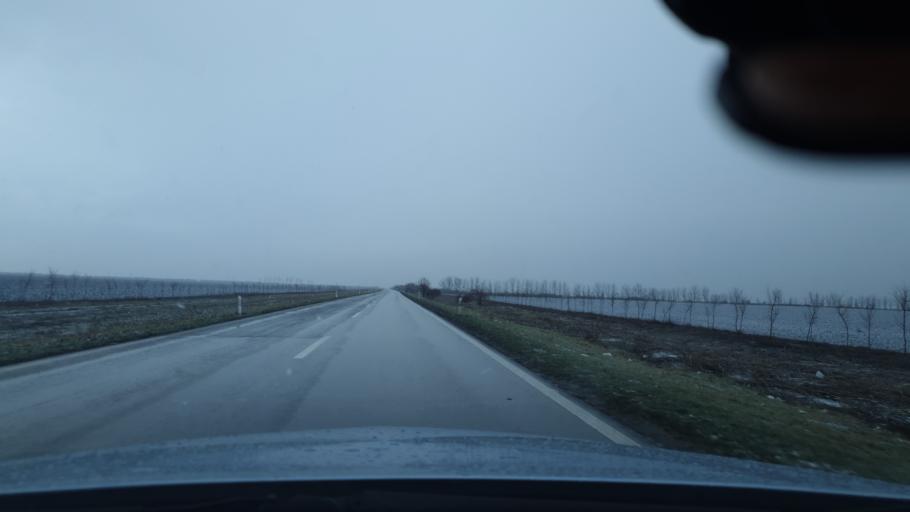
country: RS
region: Autonomna Pokrajina Vojvodina
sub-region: Juznobanatski Okrug
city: Pancevo
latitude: 44.8558
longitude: 20.7564
